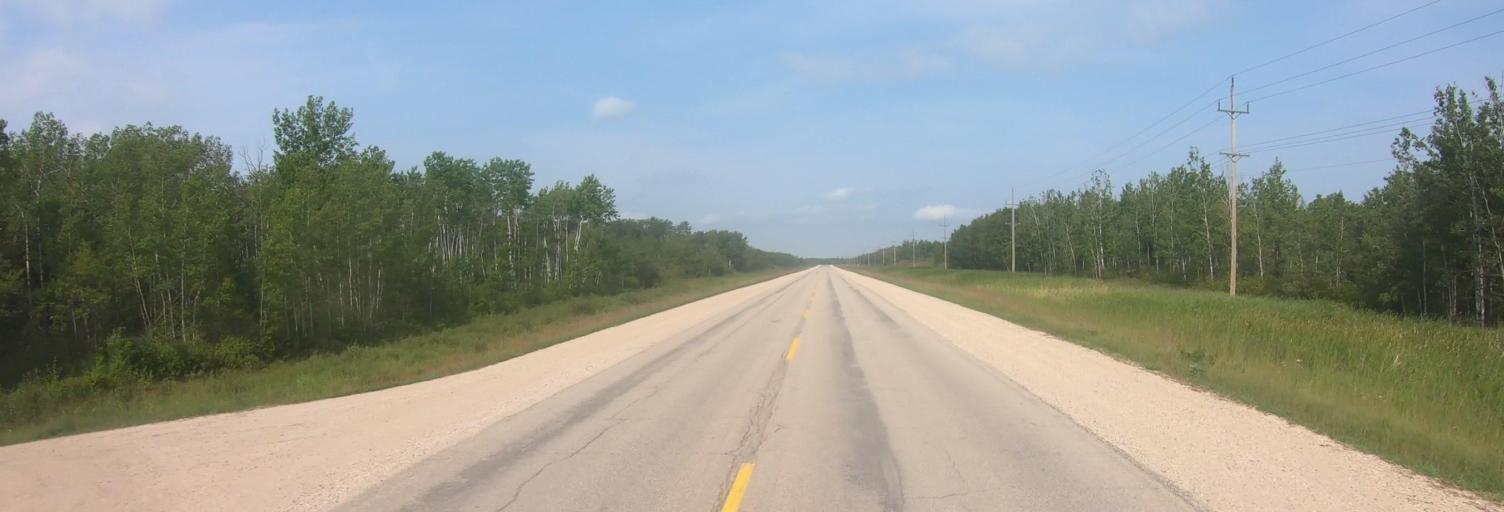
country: CA
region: Manitoba
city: Steinbach
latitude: 49.3513
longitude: -96.6524
